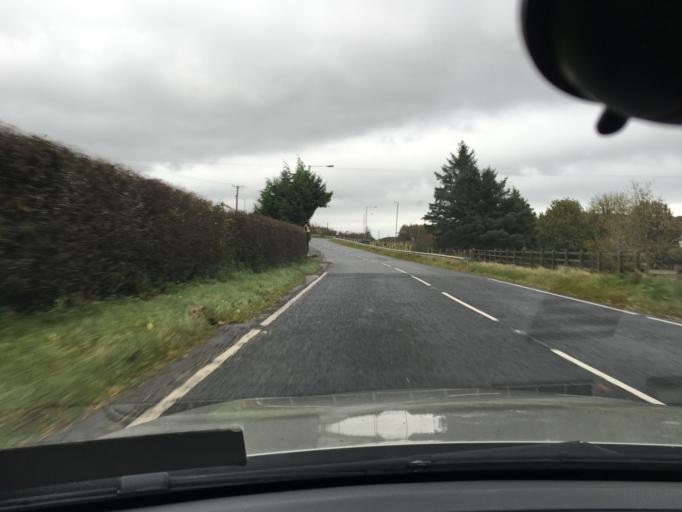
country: GB
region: Northern Ireland
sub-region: Newry and Mourne District
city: Newry
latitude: 54.1358
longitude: -6.3427
